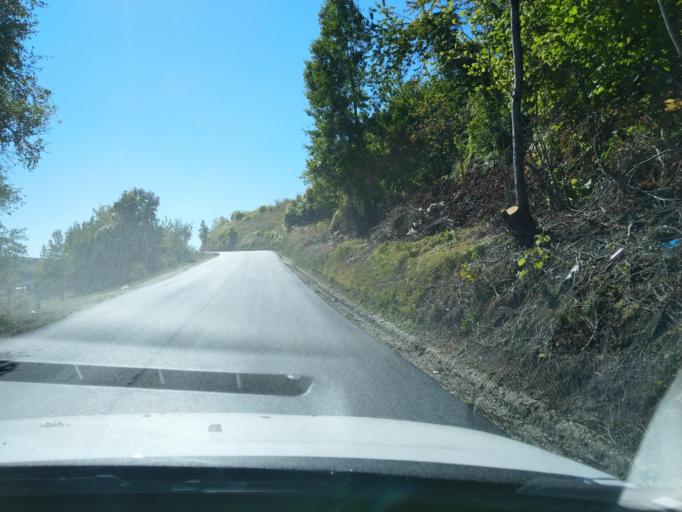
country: RS
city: Sokolovica
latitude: 43.2587
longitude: 20.2319
